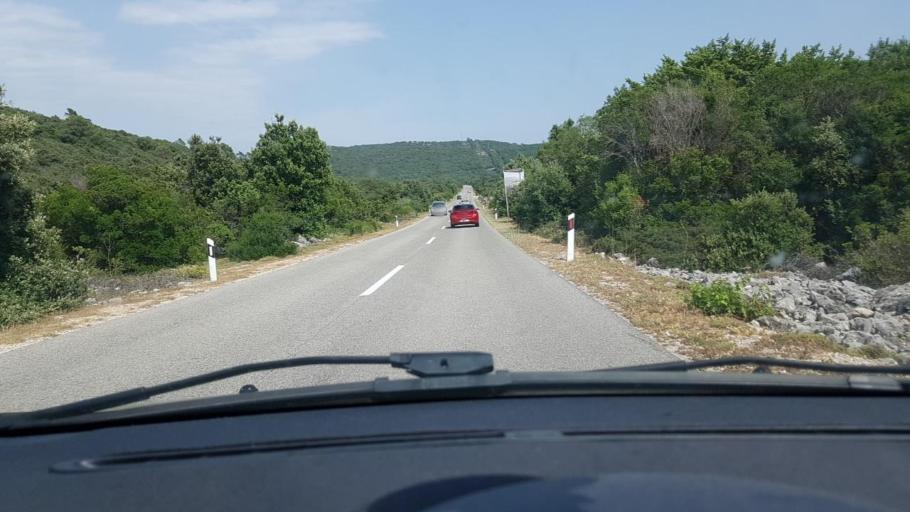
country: HR
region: Dubrovacko-Neretvanska
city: Smokvica
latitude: 42.9489
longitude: 16.9865
